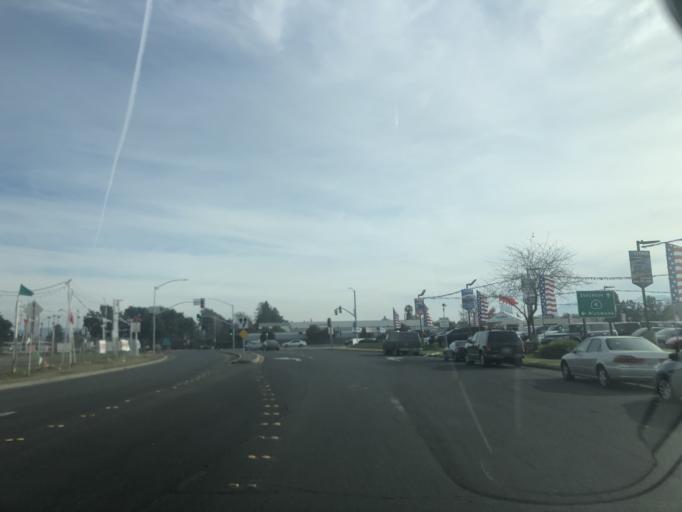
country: US
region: California
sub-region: Contra Costa County
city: Pacheco
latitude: 37.9992
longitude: -122.0541
